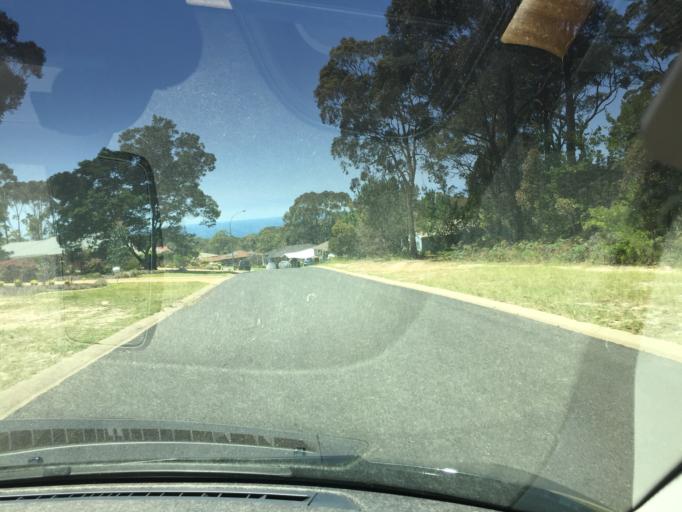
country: AU
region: New South Wales
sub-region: Bega Valley
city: Merimbula
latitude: -36.8537
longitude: 149.9251
